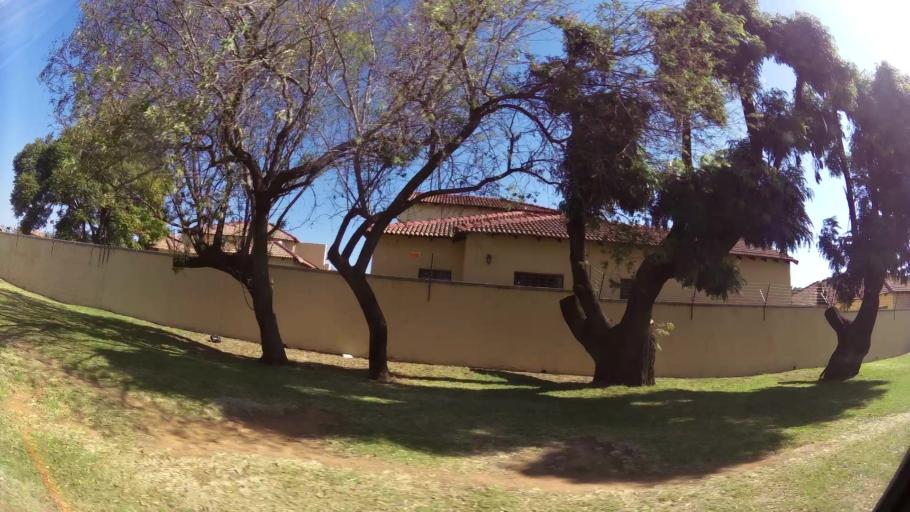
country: ZA
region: Gauteng
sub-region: City of Johannesburg Metropolitan Municipality
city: Midrand
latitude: -25.9679
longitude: 28.1155
